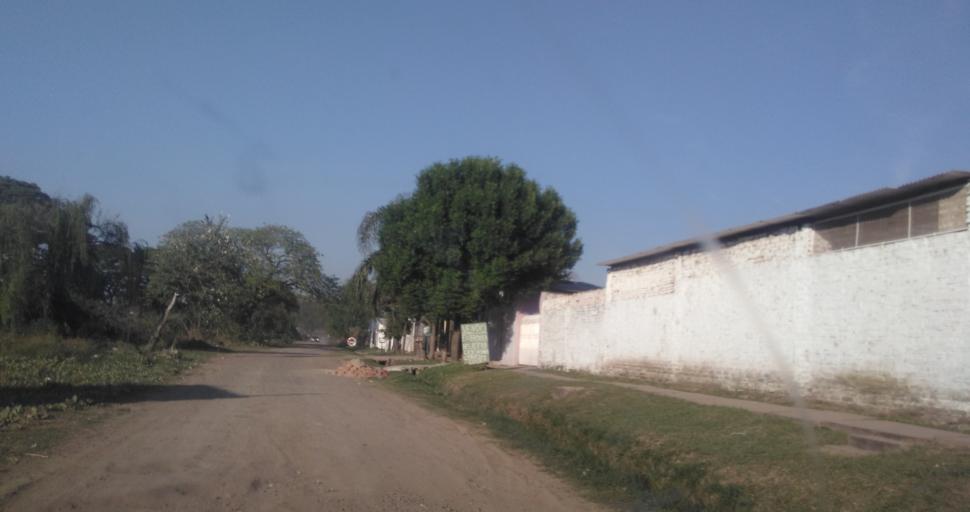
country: AR
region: Chaco
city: Fontana
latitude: -27.4113
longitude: -59.0313
